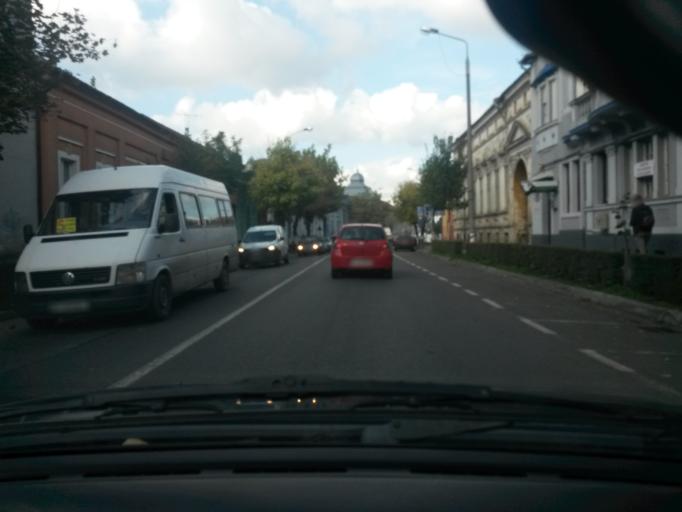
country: RO
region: Mures
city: Targu-Mures
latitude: 46.5498
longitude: 24.5648
